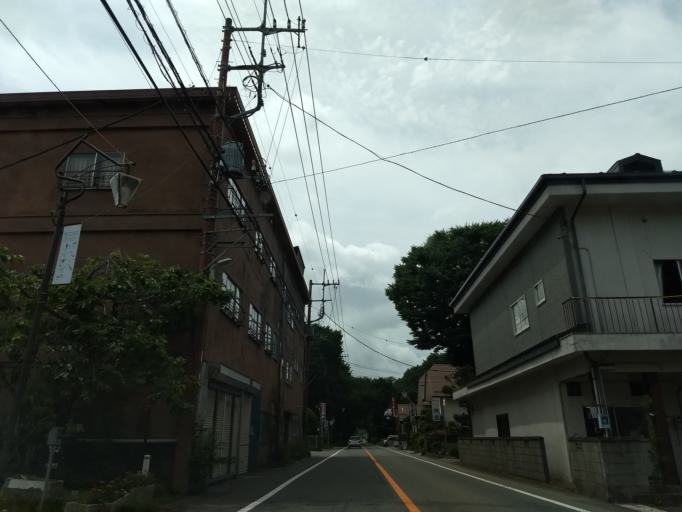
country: JP
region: Shizuoka
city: Gotemba
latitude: 35.4242
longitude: 138.9043
